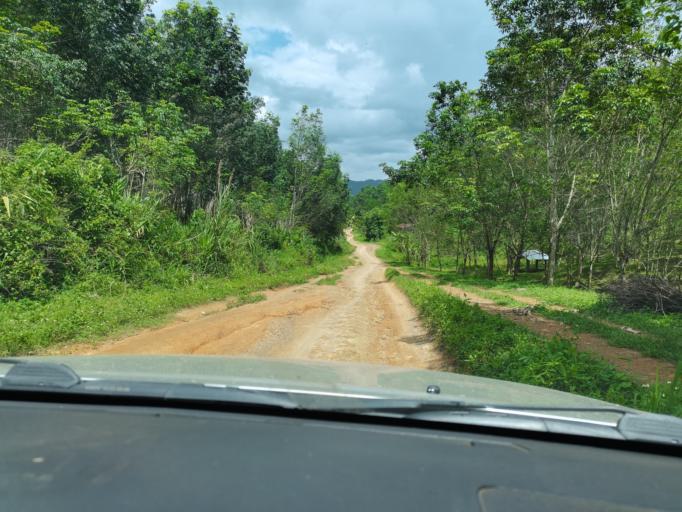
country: LA
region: Loungnamtha
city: Muang Long
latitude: 20.6853
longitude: 101.0449
